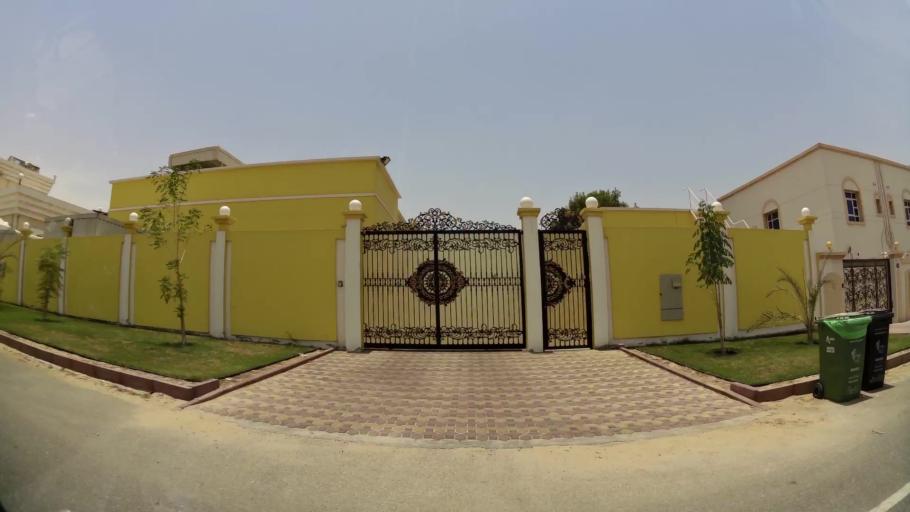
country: AE
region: Ash Shariqah
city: Sharjah
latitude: 25.2097
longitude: 55.3774
